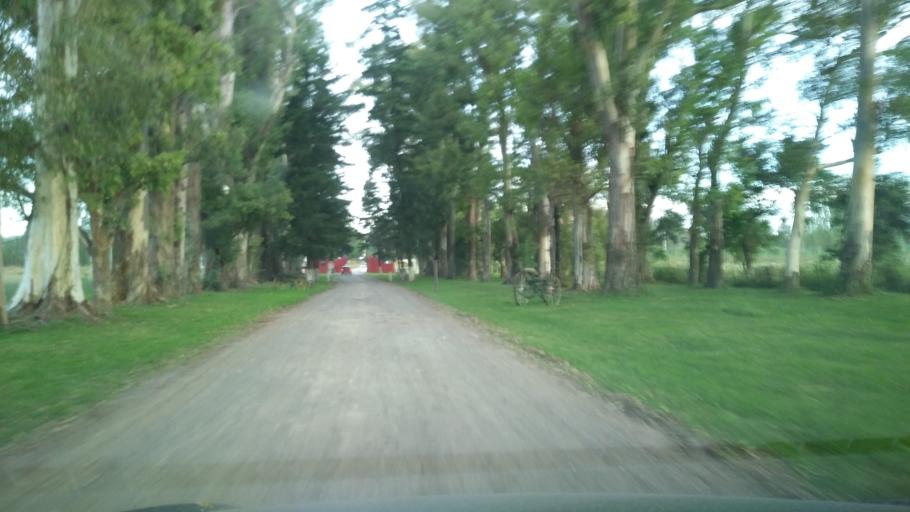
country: AR
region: Buenos Aires
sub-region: Partido de Lujan
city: Lujan
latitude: -34.5923
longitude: -59.1509
